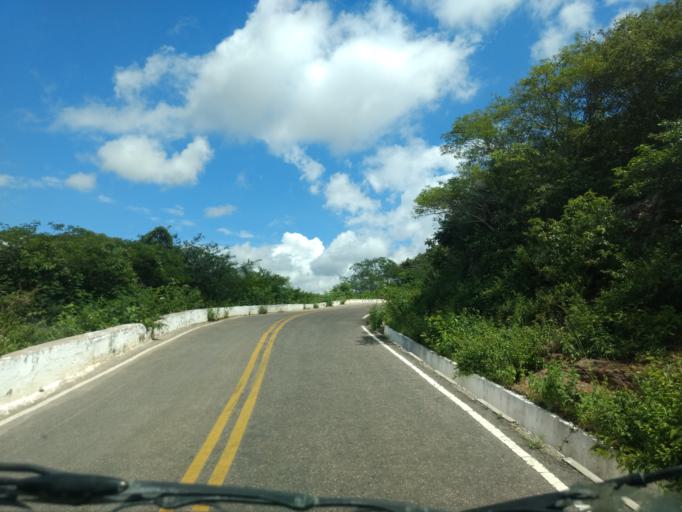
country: BR
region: Ceara
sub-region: Crateus
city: Crateus
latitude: -5.2394
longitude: -40.9262
